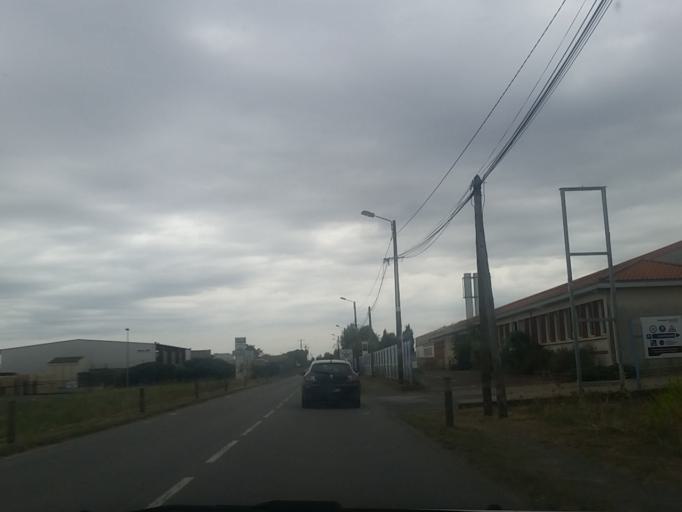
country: FR
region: Pays de la Loire
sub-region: Departement de la Loire-Atlantique
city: La Remaudiere
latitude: 47.2361
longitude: -1.2166
